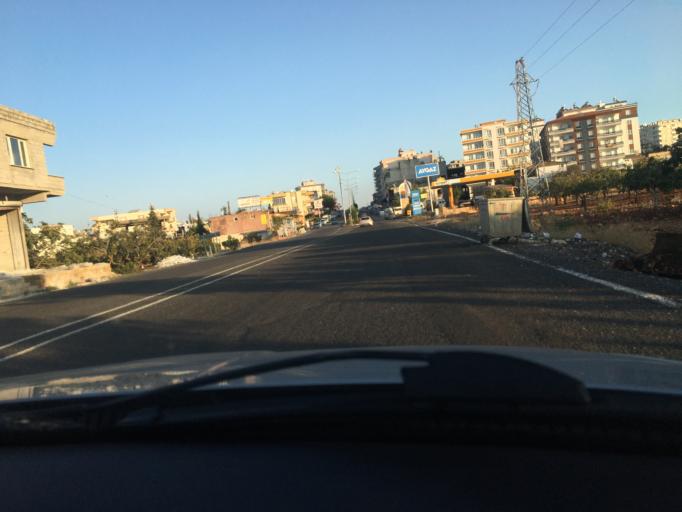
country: TR
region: Sanliurfa
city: Halfeti
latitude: 37.2324
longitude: 37.9407
